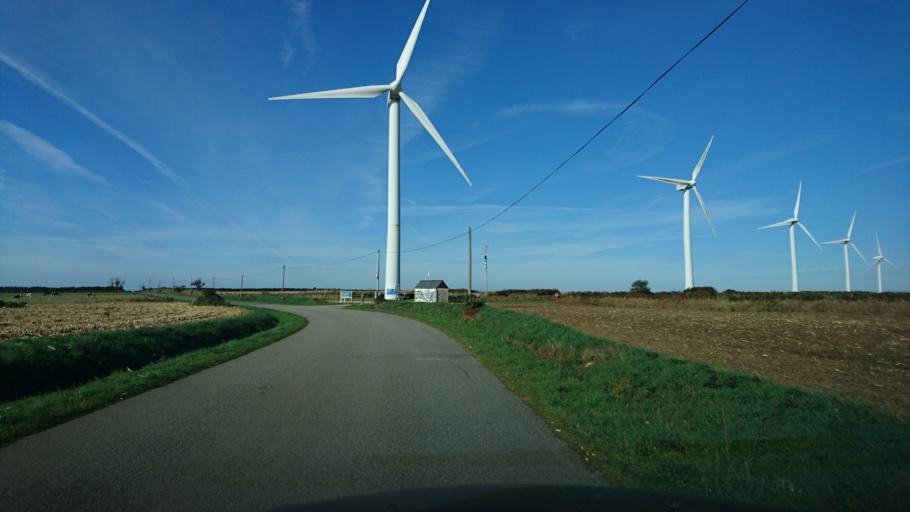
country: FR
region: Brittany
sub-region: Departement du Finistere
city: Plouarzel
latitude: 48.4276
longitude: -4.7465
